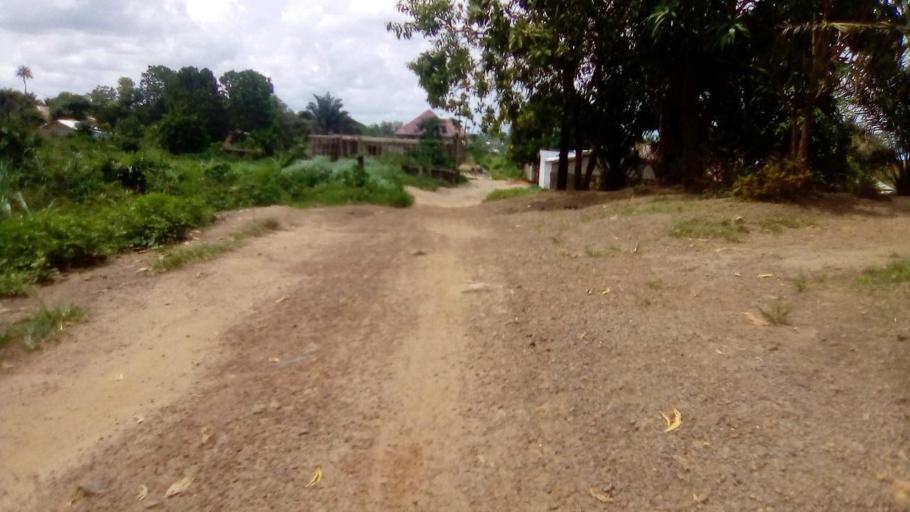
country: SL
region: Southern Province
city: Bo
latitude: 7.9381
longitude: -11.7463
